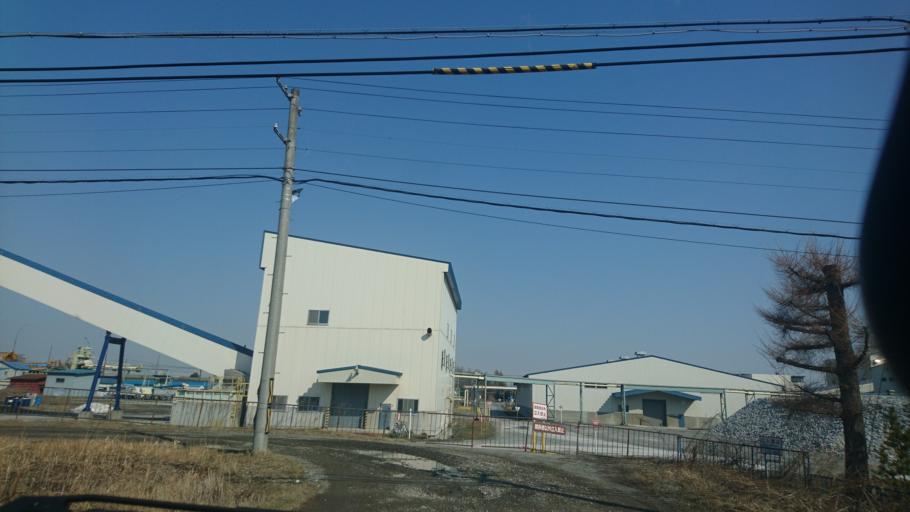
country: JP
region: Hokkaido
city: Obihiro
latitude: 42.9203
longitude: 143.0759
